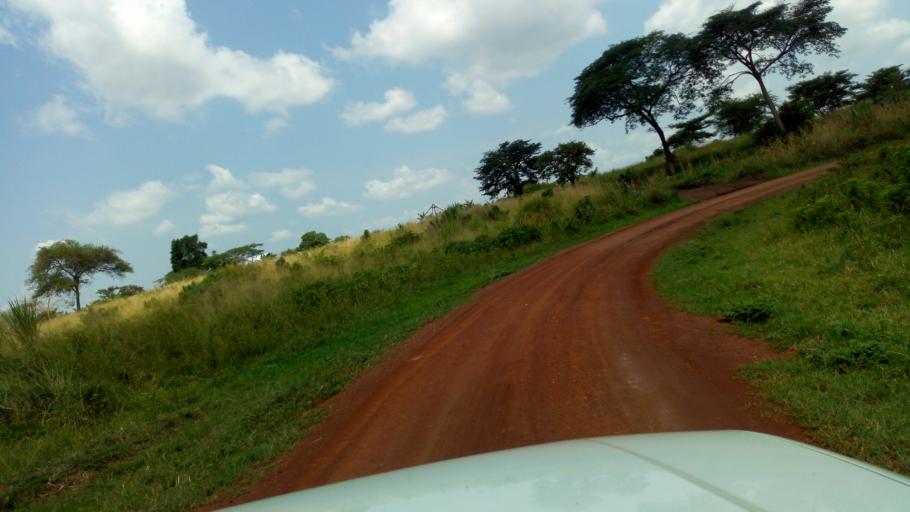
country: UG
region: Western Region
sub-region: Masindi District
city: Masindi
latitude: 1.7583
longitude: 31.8587
